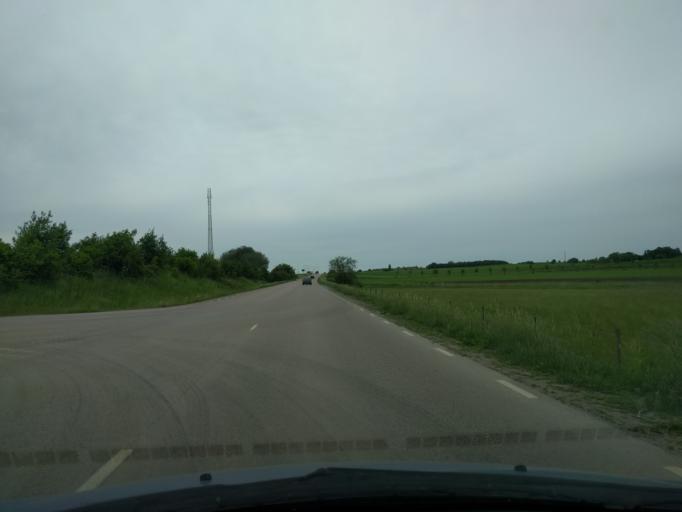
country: SE
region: Skane
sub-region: Malmo
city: Oxie
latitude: 55.5554
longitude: 13.1107
